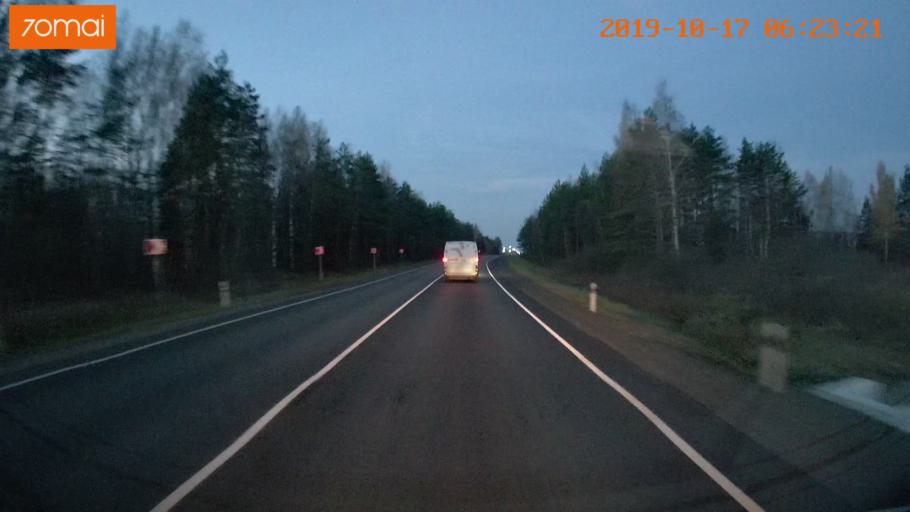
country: RU
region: Ivanovo
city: Lezhnevo
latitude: 56.7838
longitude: 40.8501
